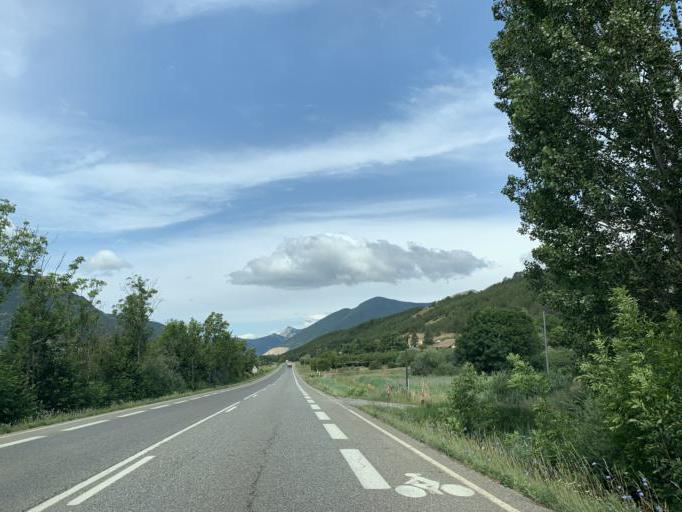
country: FR
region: Provence-Alpes-Cote d'Azur
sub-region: Departement des Hautes-Alpes
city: La Roche-des-Arnauds
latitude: 44.5490
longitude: 5.9796
